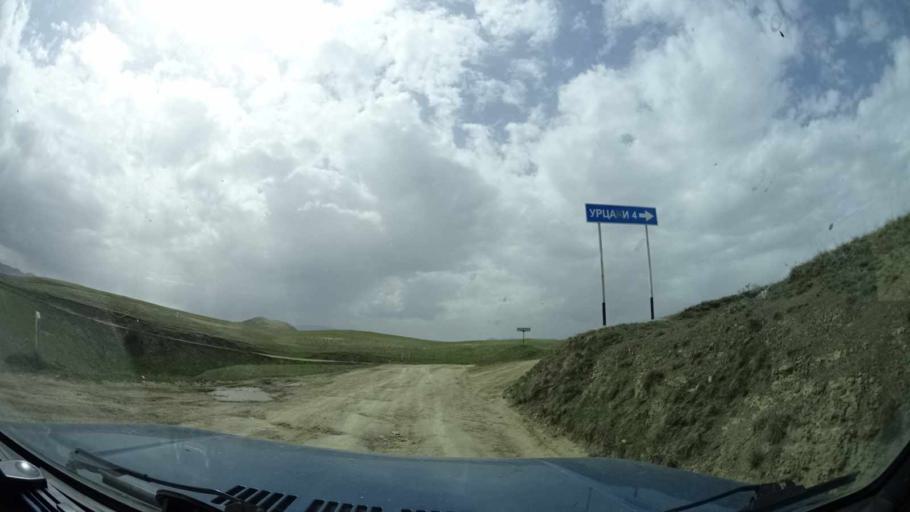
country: RU
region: Dagestan
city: Kubachi
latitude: 42.0840
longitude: 47.5585
